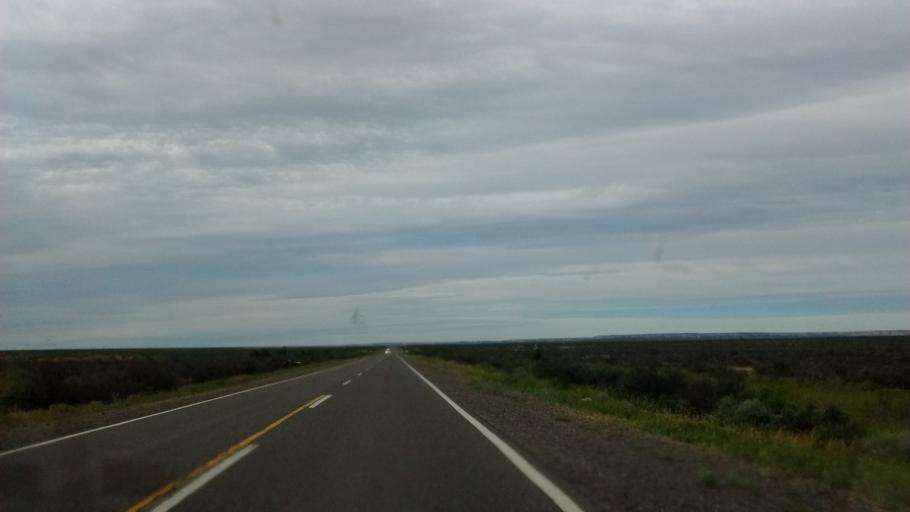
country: AR
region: Rio Negro
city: Catriel
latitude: -38.0456
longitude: -67.9189
